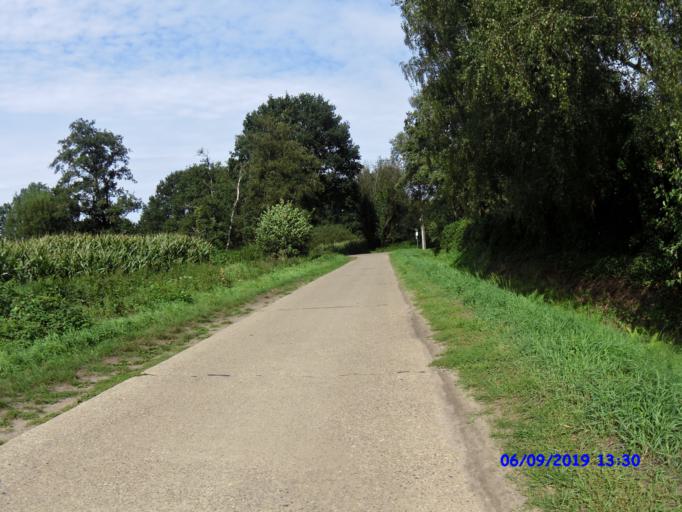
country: BE
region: Flanders
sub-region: Provincie Antwerpen
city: Kasterlee
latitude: 51.2260
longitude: 4.9799
